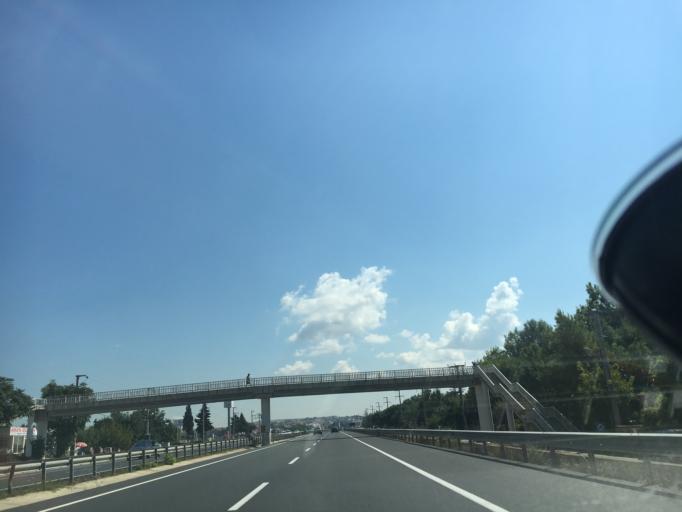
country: TR
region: Istanbul
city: Canta
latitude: 41.0544
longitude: 28.0646
